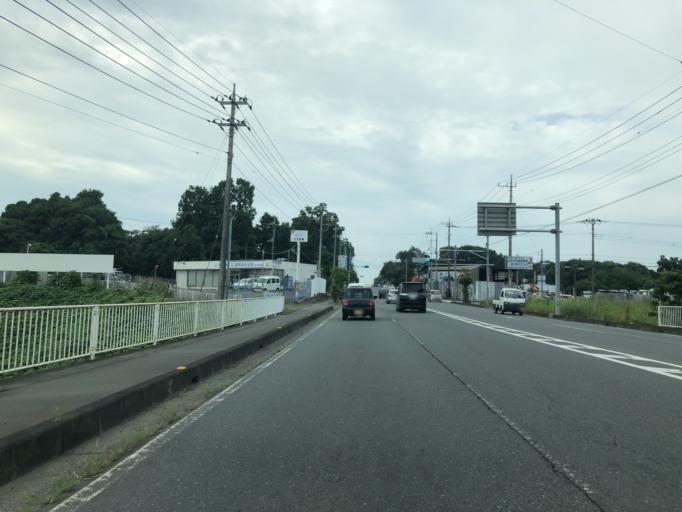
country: JP
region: Saitama
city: Fukiage-fujimi
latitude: 36.0465
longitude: 139.4134
